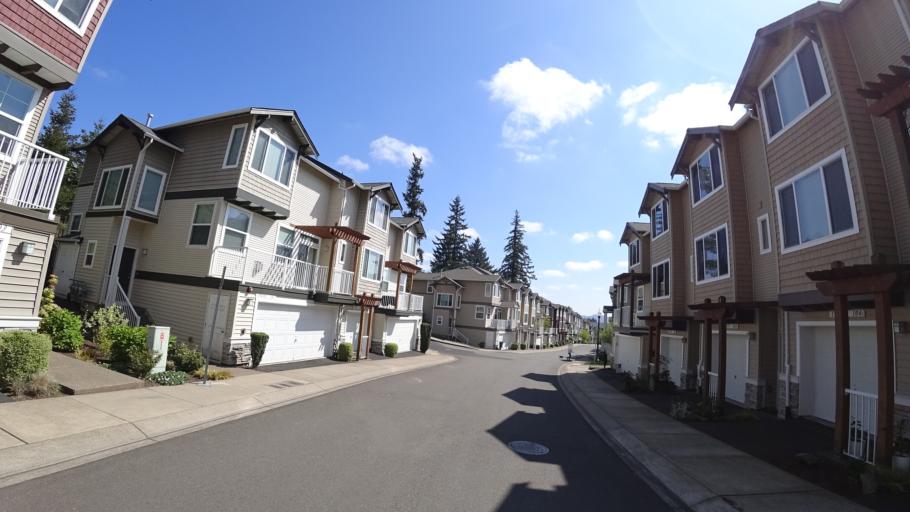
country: US
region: Oregon
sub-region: Washington County
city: King City
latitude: 45.4325
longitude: -122.8347
